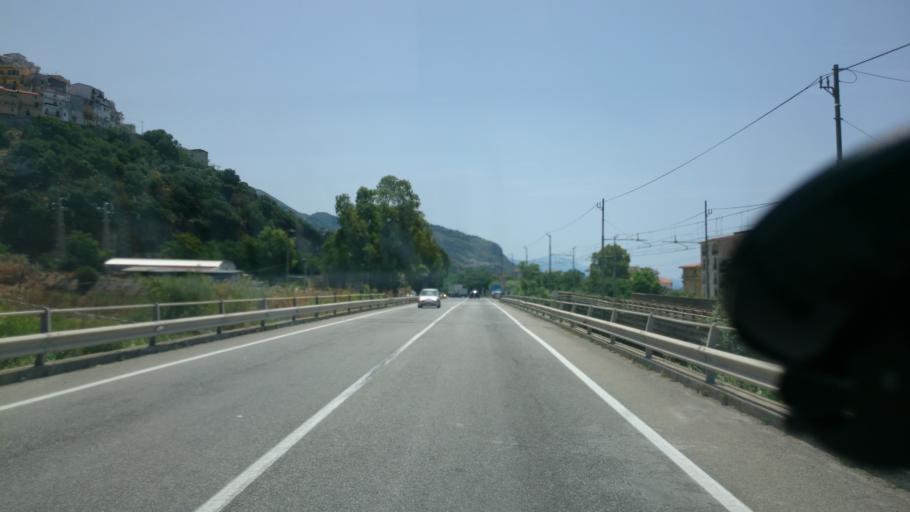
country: IT
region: Calabria
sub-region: Provincia di Cosenza
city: Cetraro Marina
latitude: 39.5192
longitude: 15.9333
